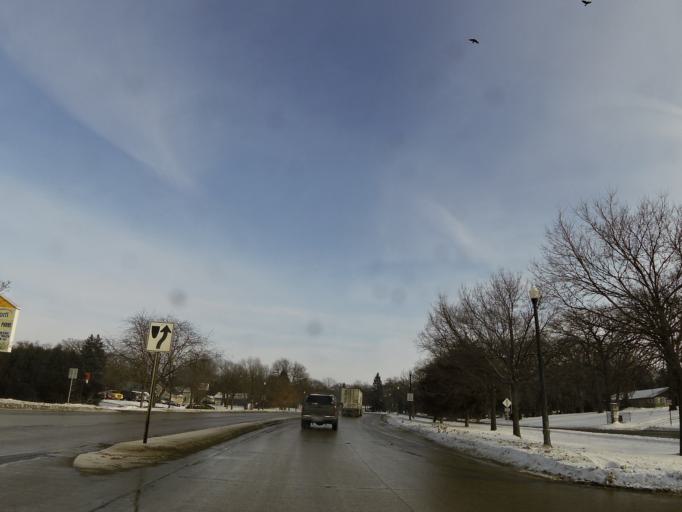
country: US
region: Minnesota
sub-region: McLeod County
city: Hutchinson
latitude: 44.8808
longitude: -94.3729
